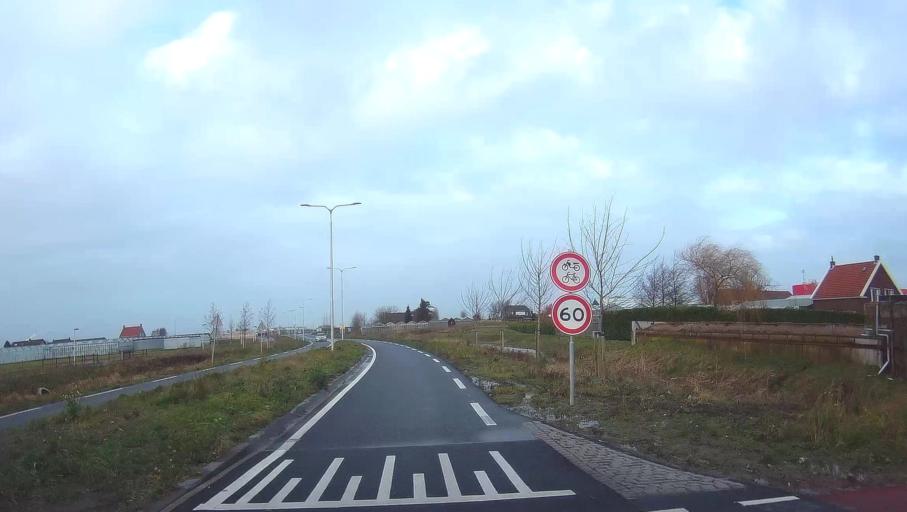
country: NL
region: South Holland
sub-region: Gemeente Pijnacker-Nootdorp
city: Pijnacker
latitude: 52.0126
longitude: 4.4146
